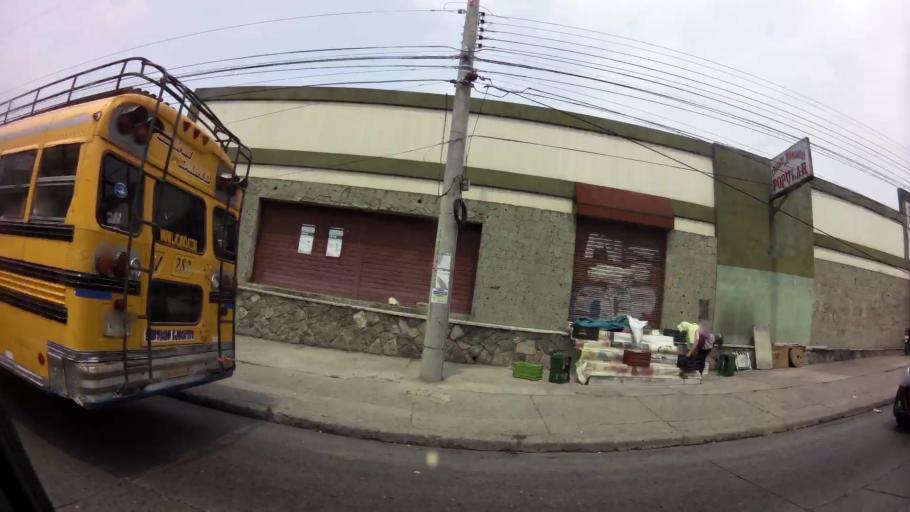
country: HN
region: Francisco Morazan
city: Tegucigalpa
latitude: 14.0822
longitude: -87.2094
